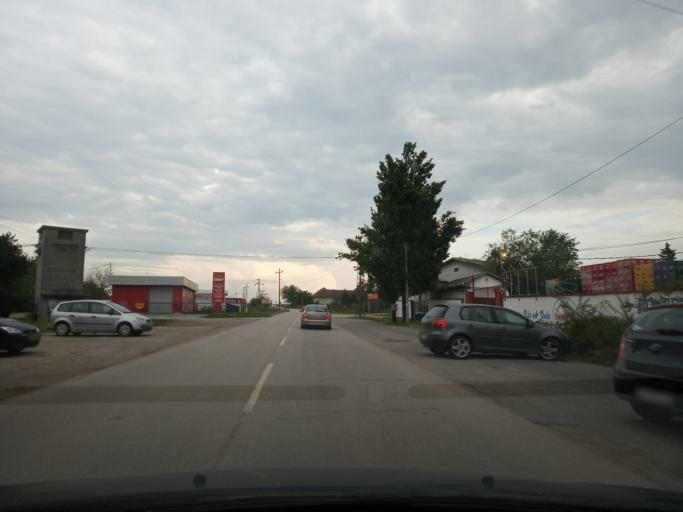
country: RS
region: Autonomna Pokrajina Vojvodina
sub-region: Juznobanatski Okrug
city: Vrsac
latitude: 45.1116
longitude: 21.3086
